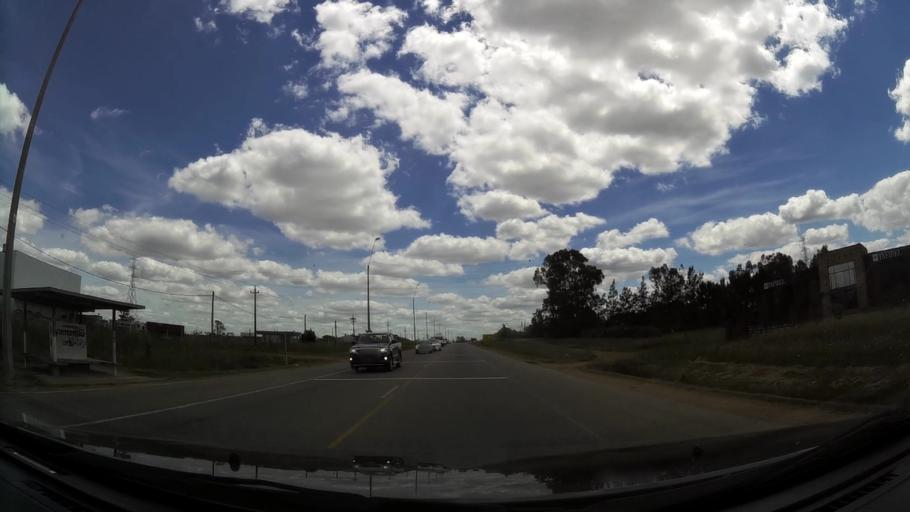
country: UY
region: Canelones
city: Colonia Nicolich
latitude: -34.7975
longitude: -56.0035
